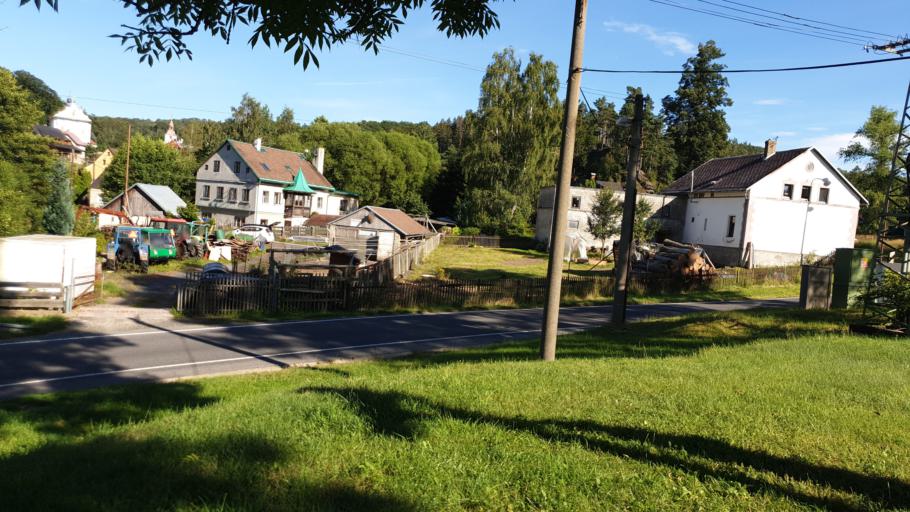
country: CZ
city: Kamenicky Senov
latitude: 50.7916
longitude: 14.4890
